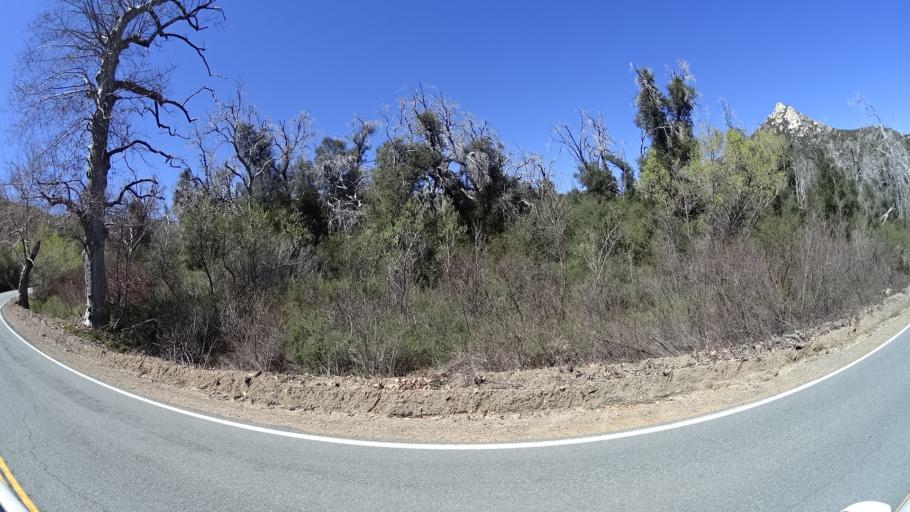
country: US
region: California
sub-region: San Diego County
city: Descanso
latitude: 32.9476
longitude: -116.5744
